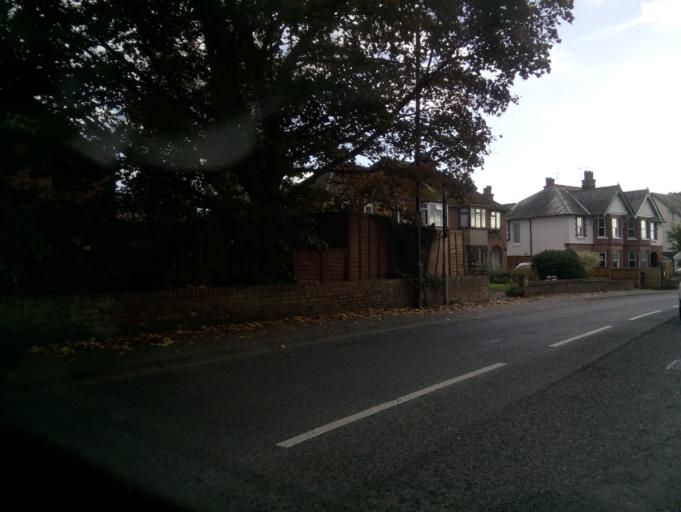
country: GB
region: England
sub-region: Herefordshire
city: Hereford
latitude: 52.0583
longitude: -2.6929
